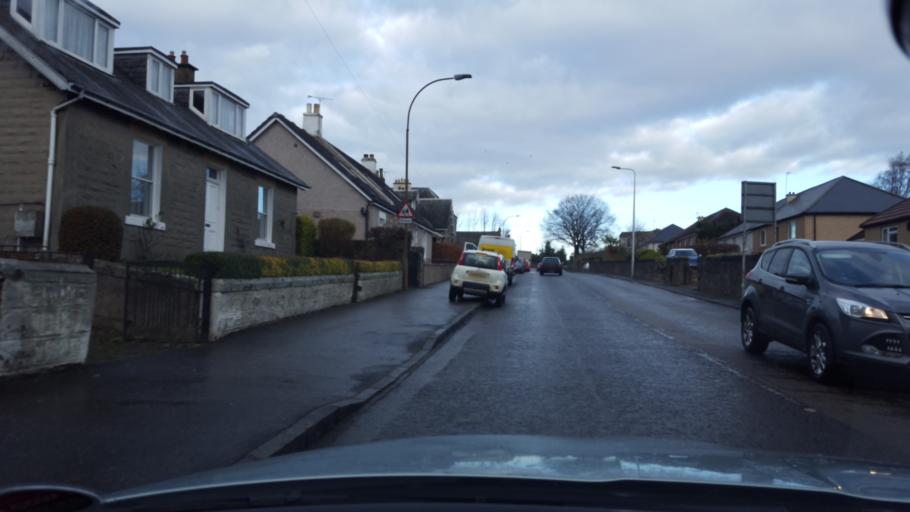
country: GB
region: Scotland
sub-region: Edinburgh
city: Kirkliston
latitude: 55.9566
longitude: -3.4022
